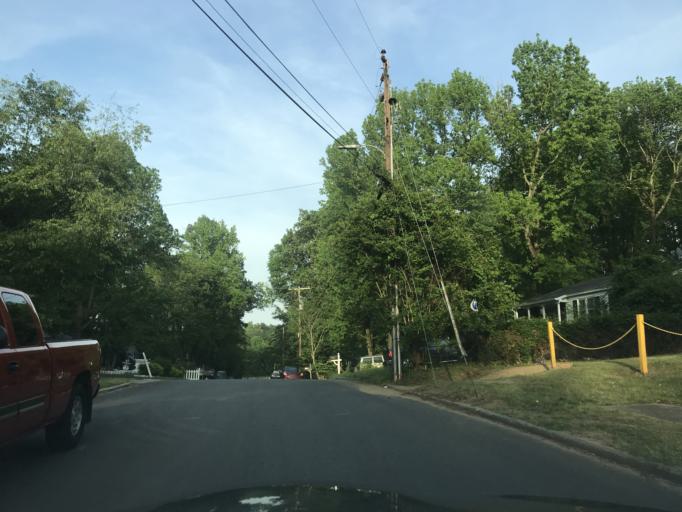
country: US
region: North Carolina
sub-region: Wake County
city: Raleigh
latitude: 35.7449
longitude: -78.6526
